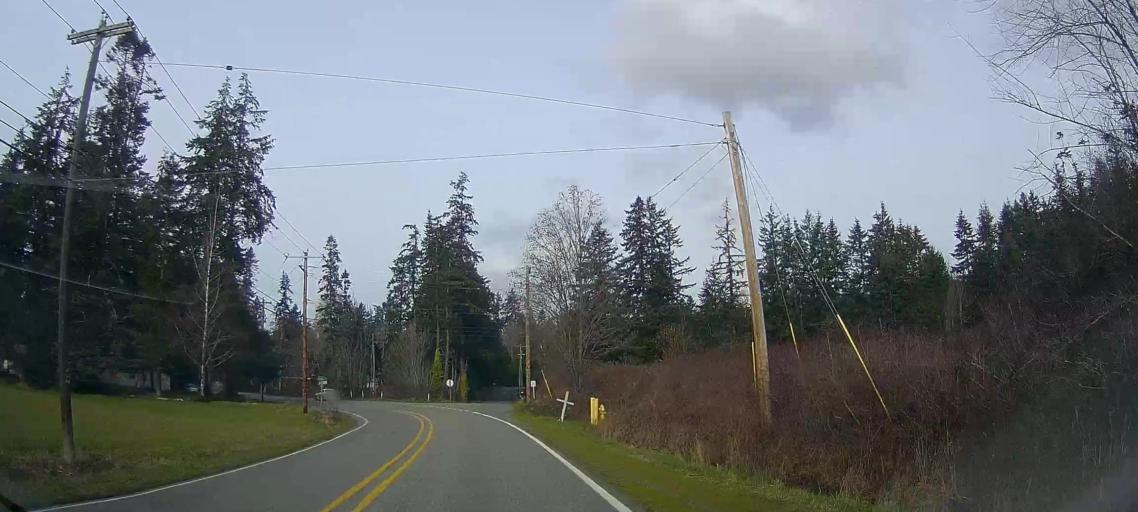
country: US
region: Washington
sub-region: Island County
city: Camano
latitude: 48.1601
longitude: -122.5166
